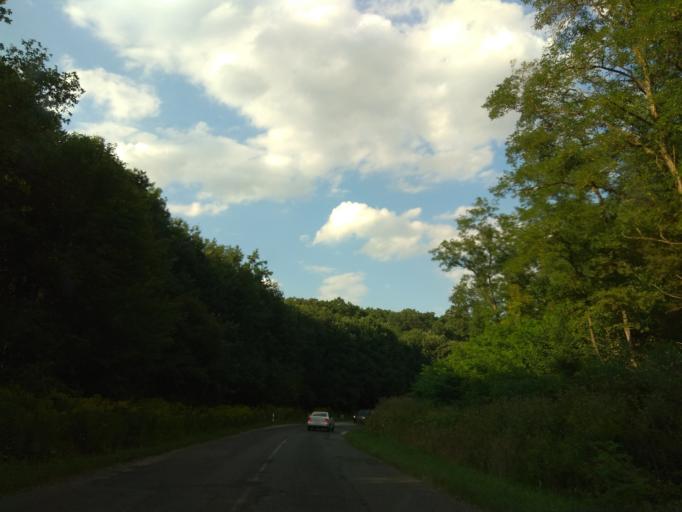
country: HU
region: Borsod-Abauj-Zemplen
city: Harsany
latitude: 47.9957
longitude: 20.7544
